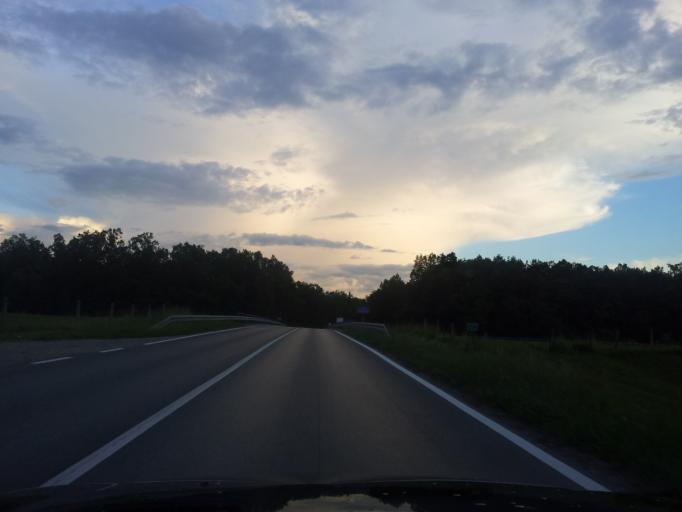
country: HR
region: Karlovacka
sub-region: Grad Karlovac
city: Karlovac
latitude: 45.5435
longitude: 15.5697
